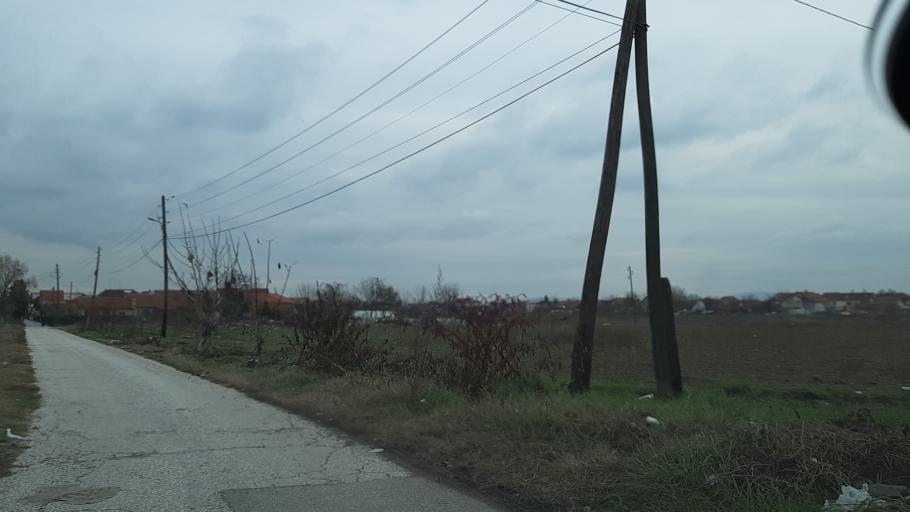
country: MK
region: Kisela Voda
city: Usje
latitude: 41.9766
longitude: 21.4760
